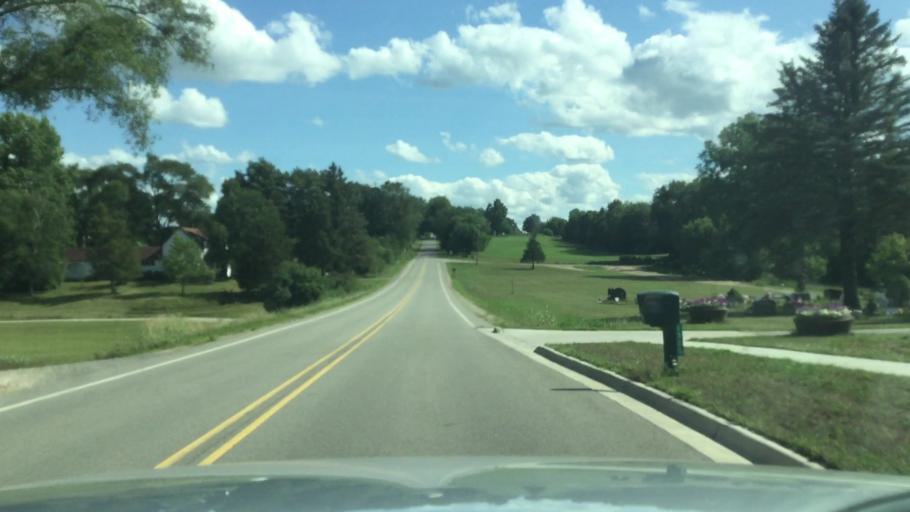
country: US
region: Michigan
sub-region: Ionia County
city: Belding
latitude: 43.0803
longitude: -85.2281
